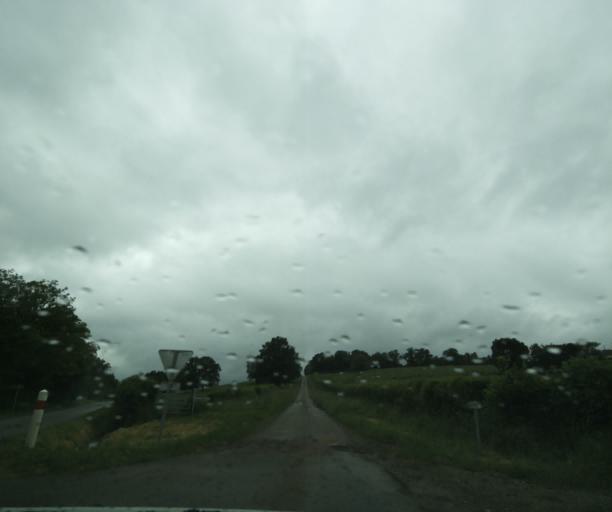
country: FR
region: Bourgogne
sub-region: Departement de Saone-et-Loire
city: Charolles
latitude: 46.4896
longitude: 4.2696
